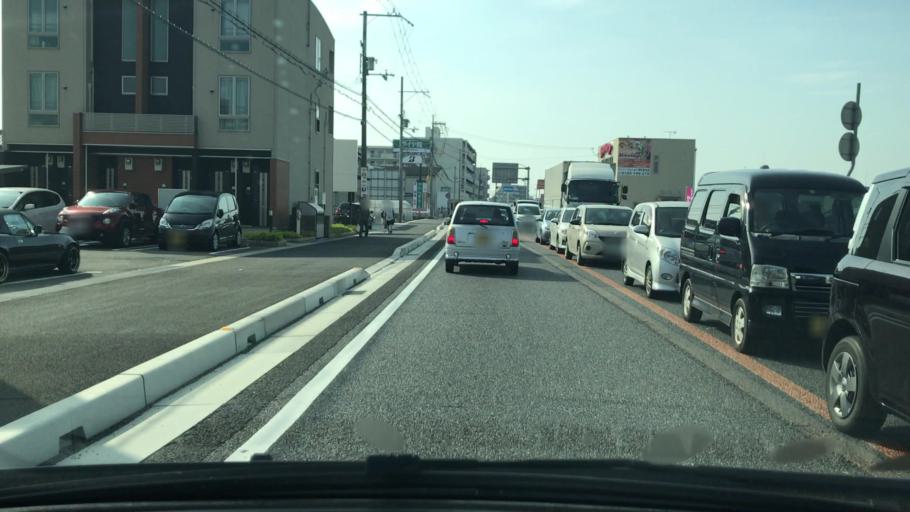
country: JP
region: Hyogo
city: Kakogawacho-honmachi
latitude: 34.7184
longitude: 134.8954
